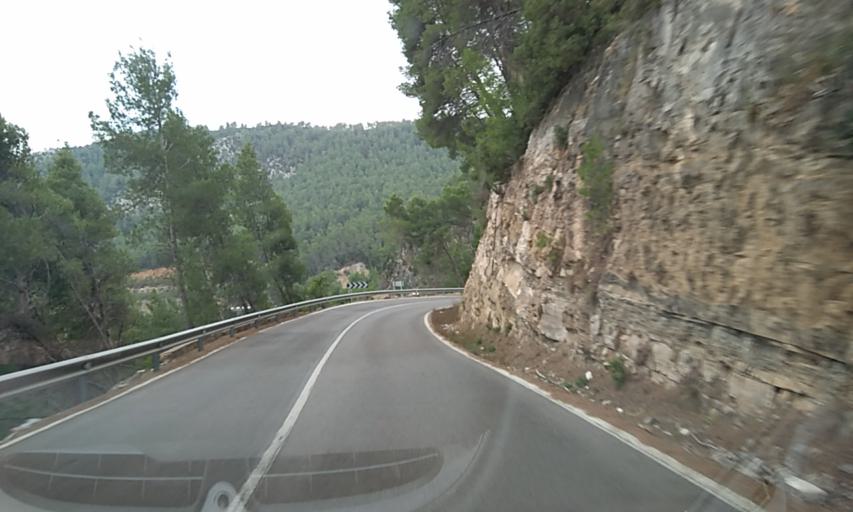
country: ES
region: Valencia
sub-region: Provincia de Castello
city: Montanejos
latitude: 40.0780
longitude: -0.5390
